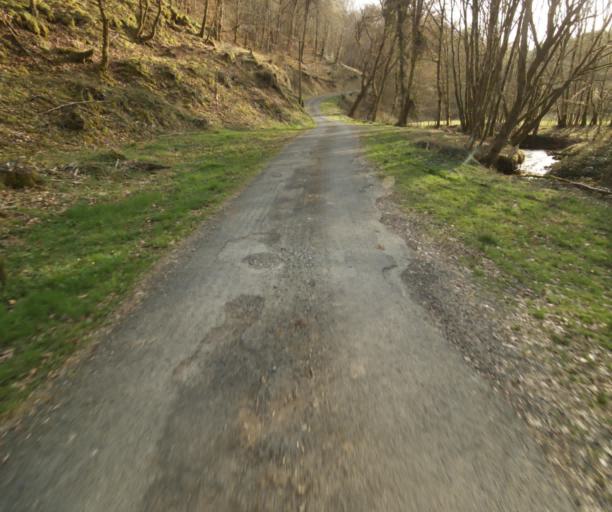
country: FR
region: Limousin
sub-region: Departement de la Correze
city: Correze
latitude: 45.3562
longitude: 1.8283
